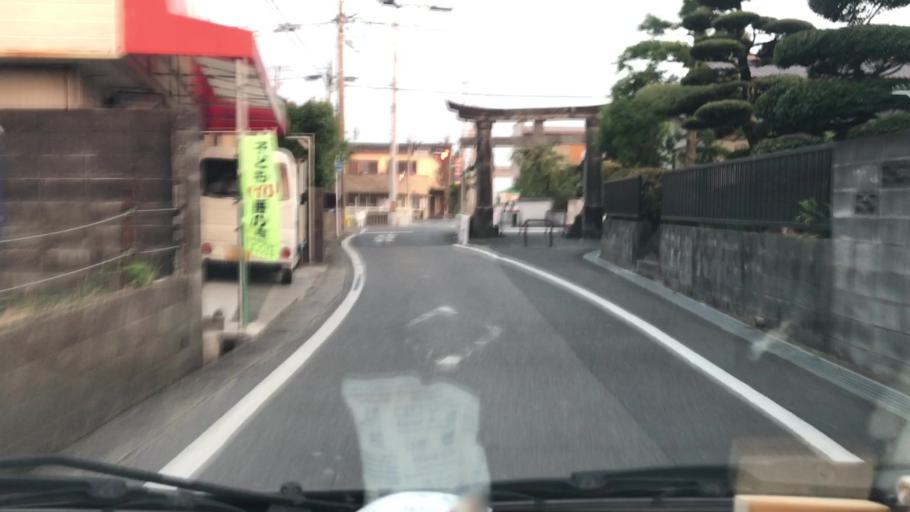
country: JP
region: Saga Prefecture
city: Saga-shi
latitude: 33.2438
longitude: 130.2578
